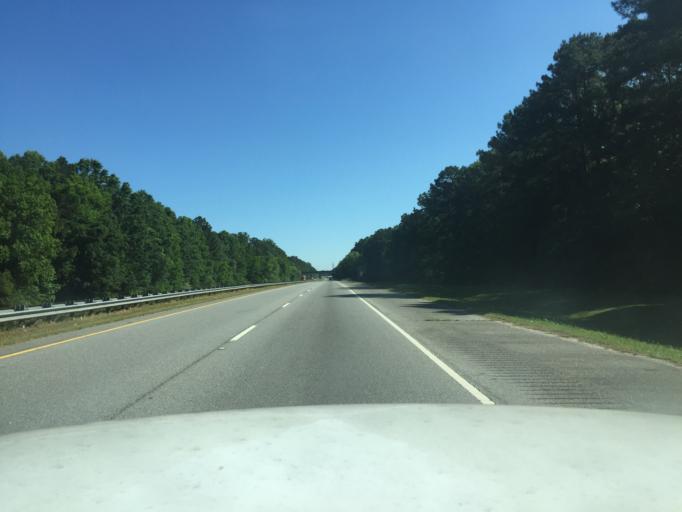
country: US
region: Georgia
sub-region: Chatham County
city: Georgetown
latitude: 32.0233
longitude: -81.1716
